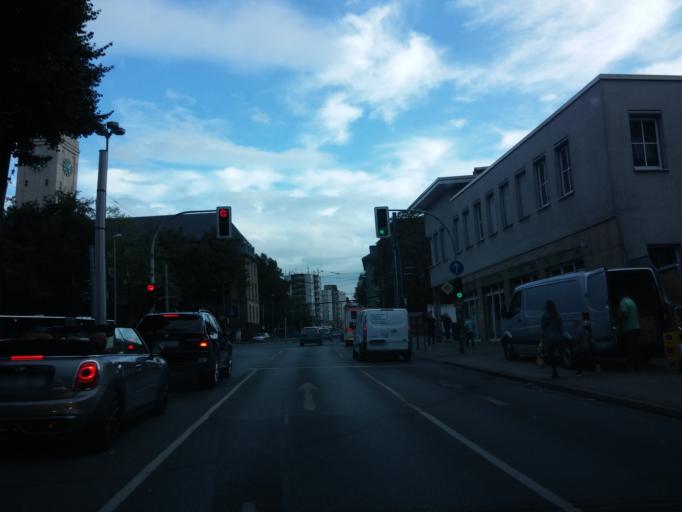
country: DE
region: North Rhine-Westphalia
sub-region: Regierungsbezirk Munster
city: Gladbeck
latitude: 51.5782
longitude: 7.0560
